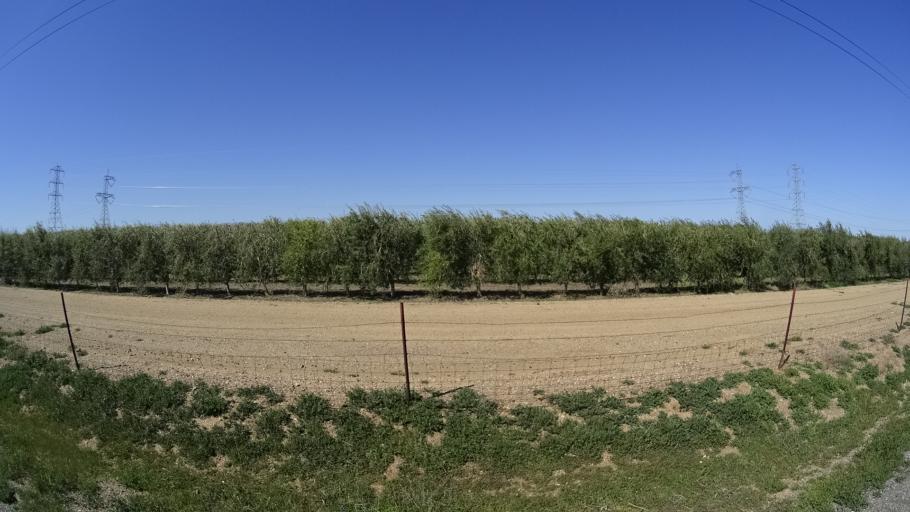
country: US
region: California
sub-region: Glenn County
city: Orland
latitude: 39.6665
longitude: -122.2723
